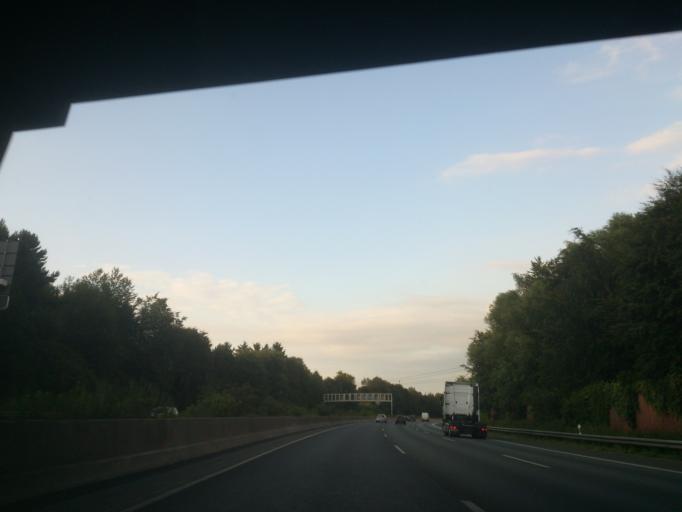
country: DE
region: North Rhine-Westphalia
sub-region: Regierungsbezirk Arnsberg
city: Holzwickede
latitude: 51.4777
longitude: 7.6069
